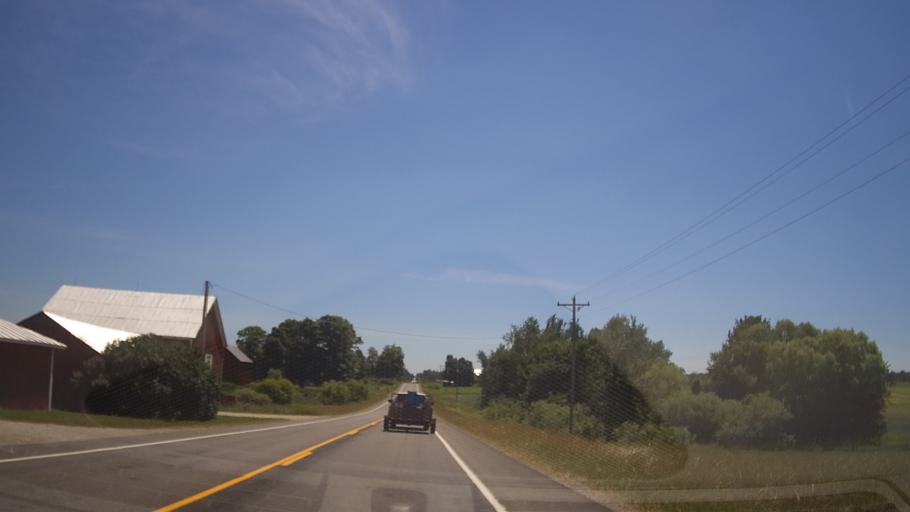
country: US
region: Michigan
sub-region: Grand Traverse County
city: Kingsley
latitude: 44.6061
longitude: -85.6965
